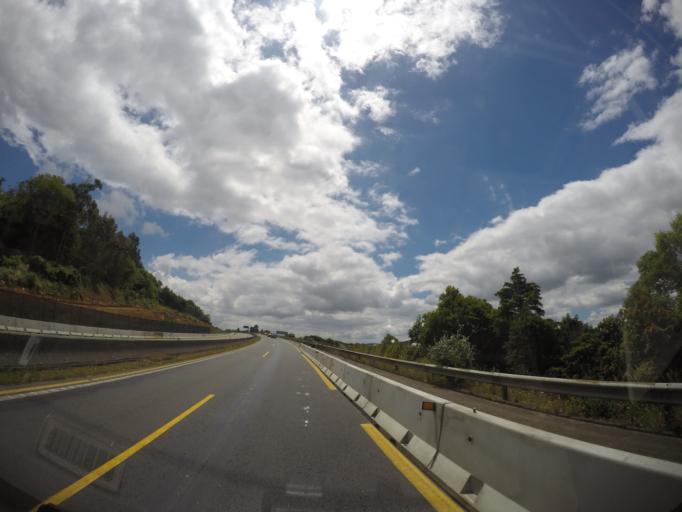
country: ES
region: Galicia
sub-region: Provincia da Coruna
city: Negreira
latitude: 42.8368
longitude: -8.7204
